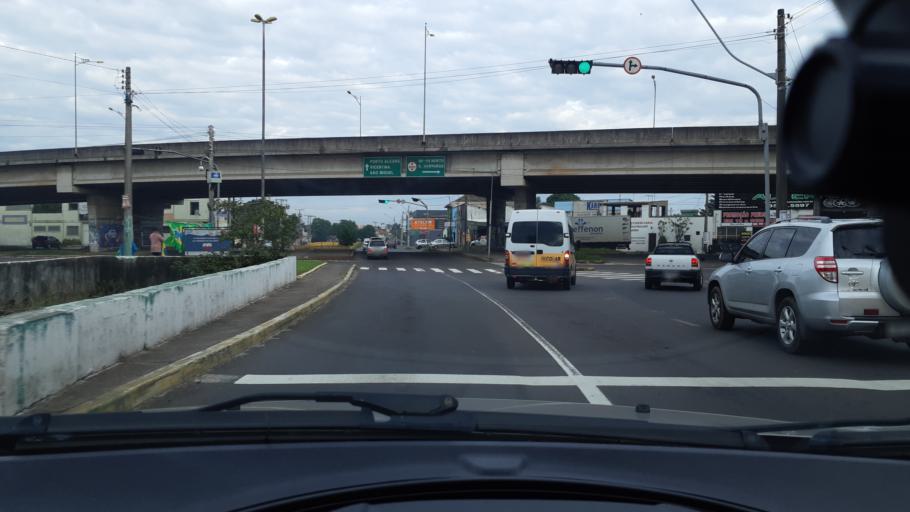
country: BR
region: Rio Grande do Sul
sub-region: Sao Leopoldo
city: Sao Leopoldo
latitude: -29.7723
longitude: -51.1534
